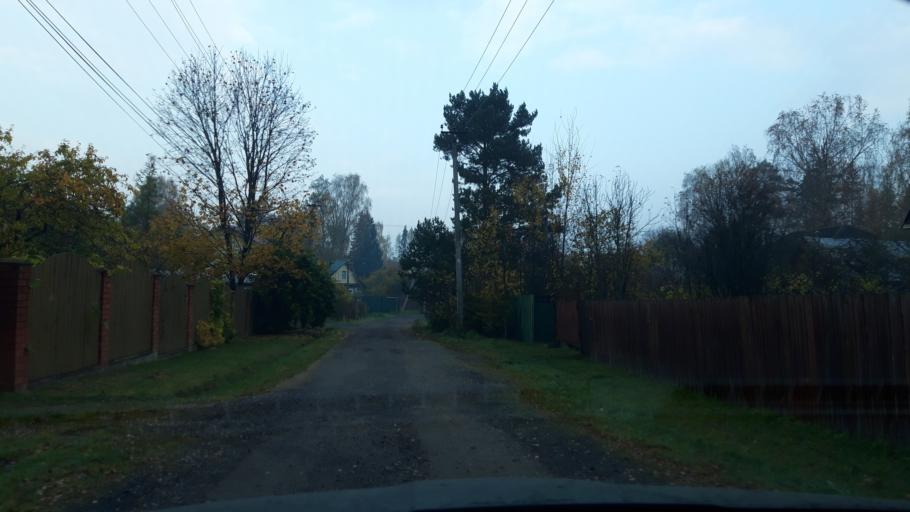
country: RU
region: Moskovskaya
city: Lozhki
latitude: 56.0519
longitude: 37.0975
